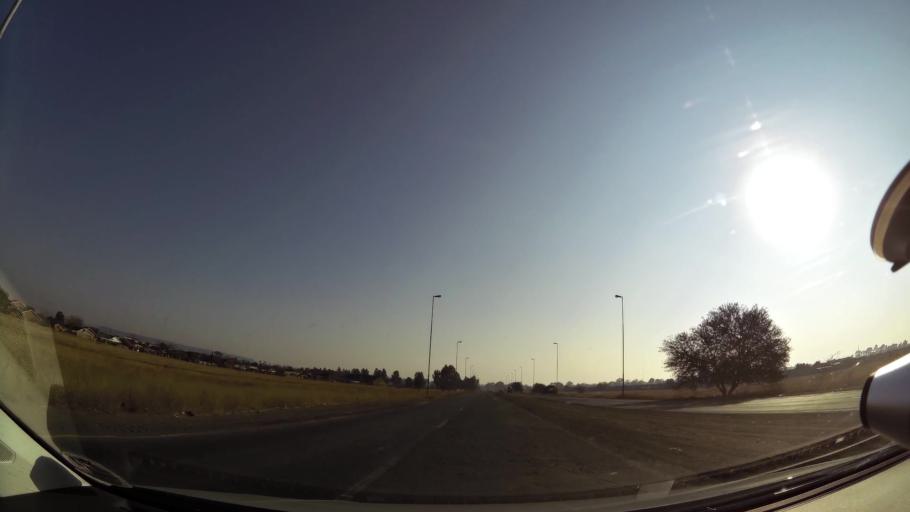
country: ZA
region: Orange Free State
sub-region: Mangaung Metropolitan Municipality
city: Bloemfontein
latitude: -29.1446
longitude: 26.2661
